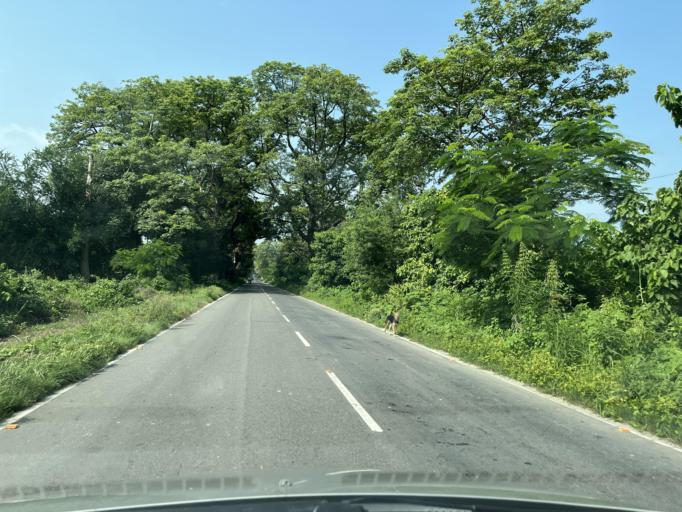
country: IN
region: Uttarakhand
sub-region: Udham Singh Nagar
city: Bazpur
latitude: 29.1913
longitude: 79.1918
